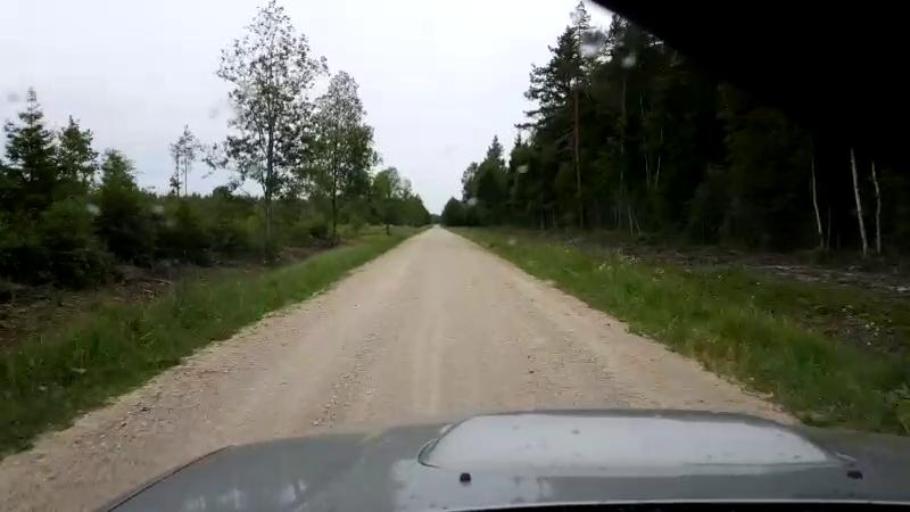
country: EE
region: Paernumaa
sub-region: Halinga vald
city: Parnu-Jaagupi
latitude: 58.5387
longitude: 24.5958
